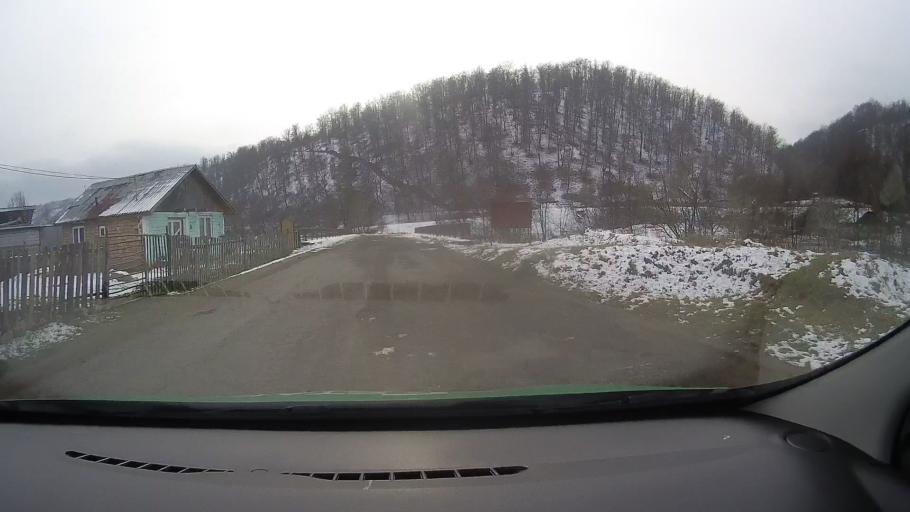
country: RO
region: Alba
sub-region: Oras Zlatna
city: Zlatna
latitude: 46.1195
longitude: 23.2057
